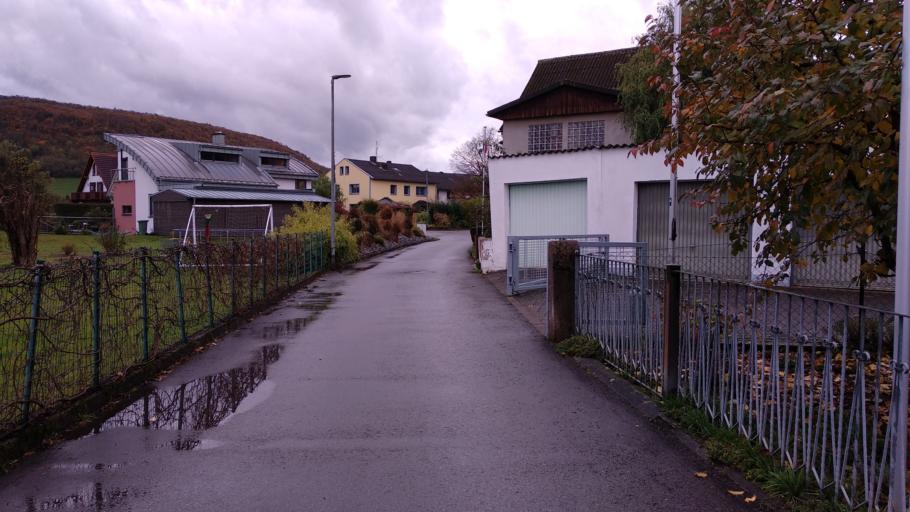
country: DE
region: North Rhine-Westphalia
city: Beverungen
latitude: 51.6617
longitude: 9.3700
